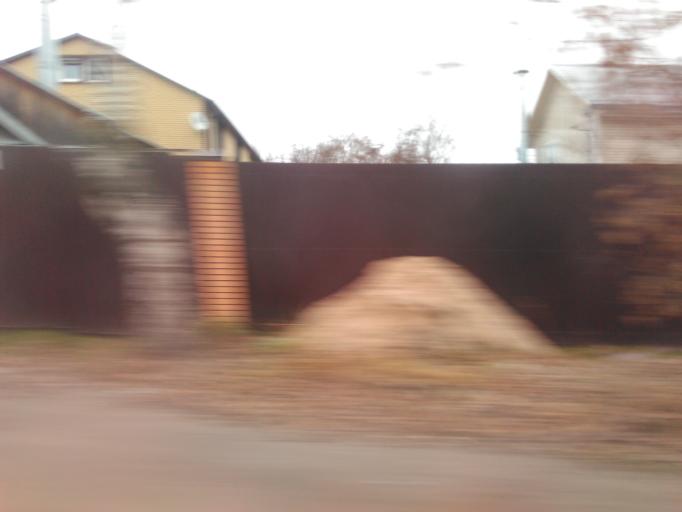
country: RU
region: Moskovskaya
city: Ashukino
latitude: 56.1672
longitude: 37.9410
